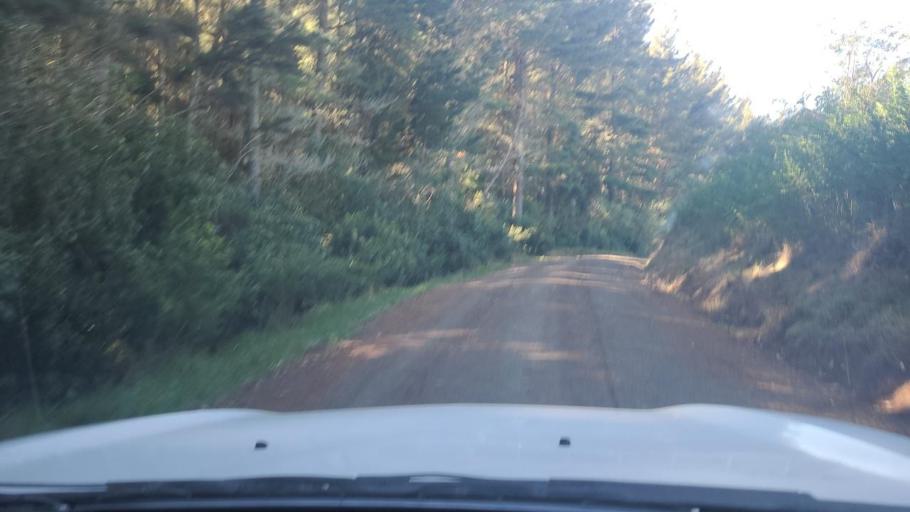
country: NZ
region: Hawke's Bay
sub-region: Napier City
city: Taradale
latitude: -39.4149
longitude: 176.4632
